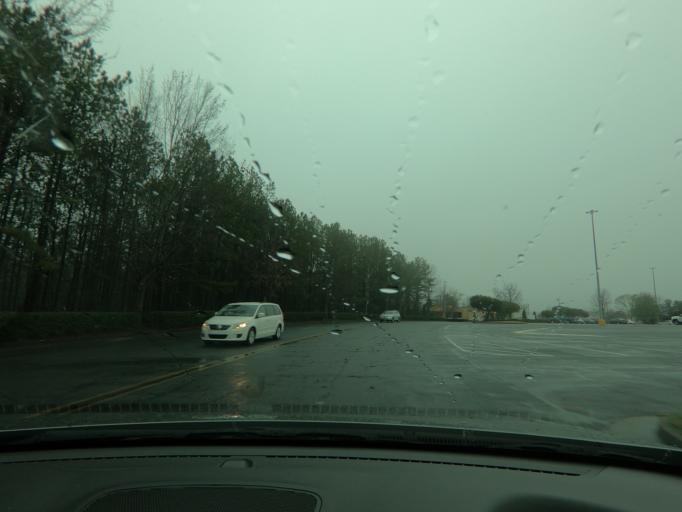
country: US
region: Georgia
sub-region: Fulton County
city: Alpharetta
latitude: 34.0484
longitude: -84.2906
